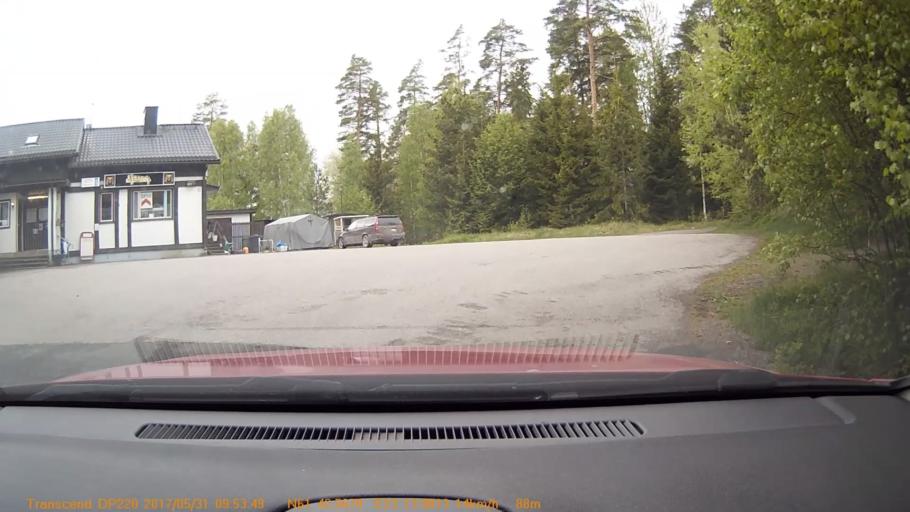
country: FI
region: Pirkanmaa
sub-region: Tampere
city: Viljakkala
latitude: 61.7095
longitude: 23.2333
